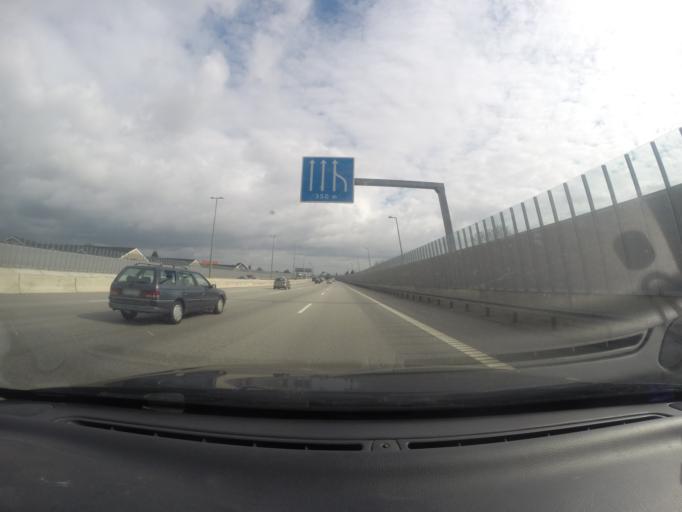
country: DK
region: Capital Region
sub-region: Rodovre Kommune
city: Rodovre
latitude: 55.6981
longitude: 12.4446
